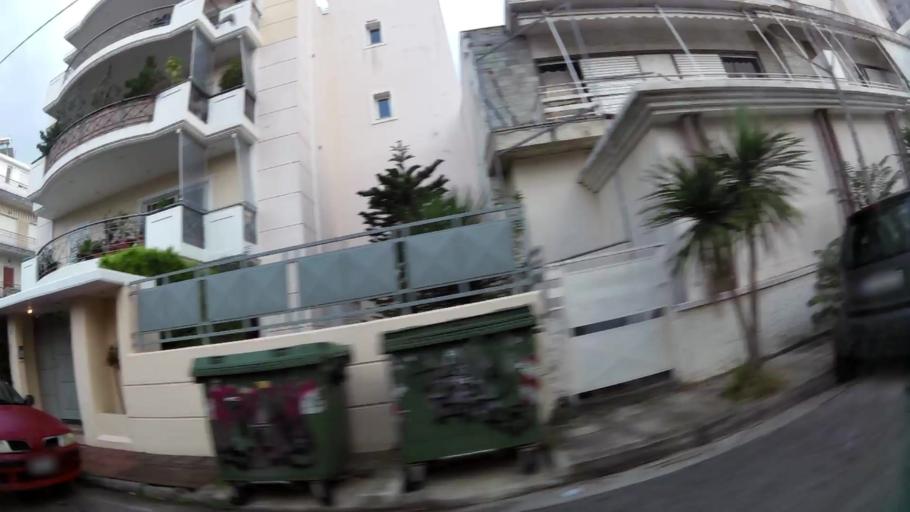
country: GR
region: Attica
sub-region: Nomarchia Athinas
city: Vrilissia
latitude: 38.0409
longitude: 23.8284
